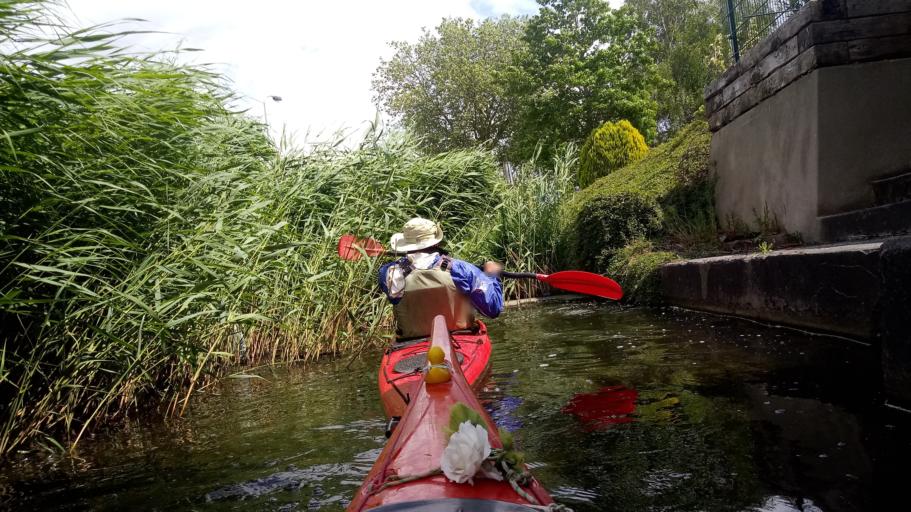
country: NL
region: North Holland
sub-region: Gemeente Enkhuizen
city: Enkhuizen
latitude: 52.6956
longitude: 5.2521
